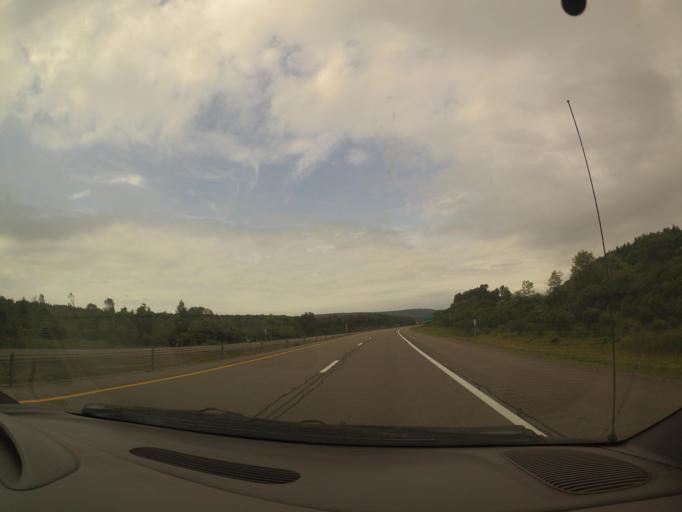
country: US
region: New York
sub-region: Allegany County
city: Alfred
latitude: 42.3094
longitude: -77.8676
